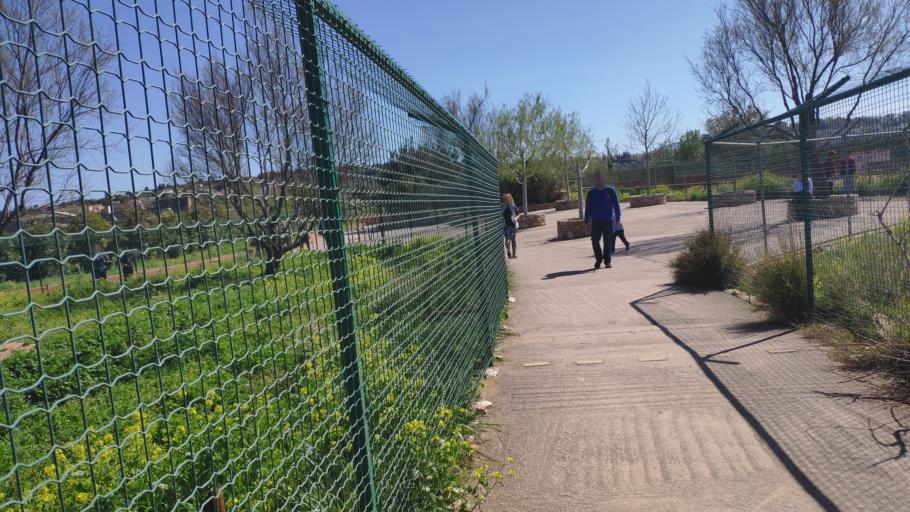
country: GR
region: Attica
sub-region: Nomarchia Anatolikis Attikis
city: Argithea
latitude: 37.9807
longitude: 23.9065
